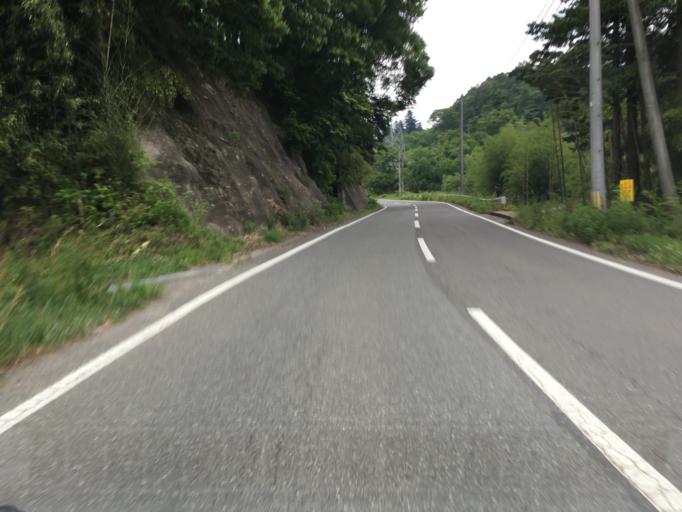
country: JP
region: Fukushima
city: Nihommatsu
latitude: 37.6212
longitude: 140.5395
